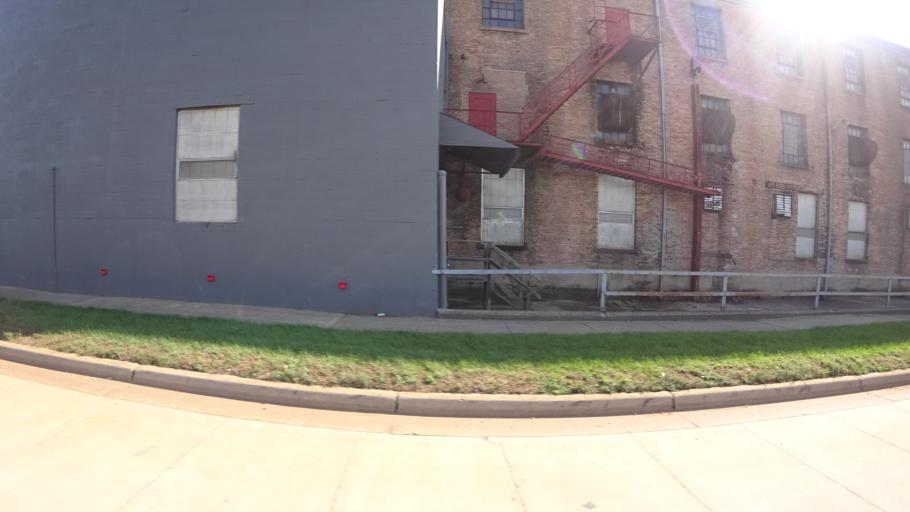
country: US
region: Michigan
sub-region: Saint Joseph County
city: Three Rivers
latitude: 41.9372
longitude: -85.6297
